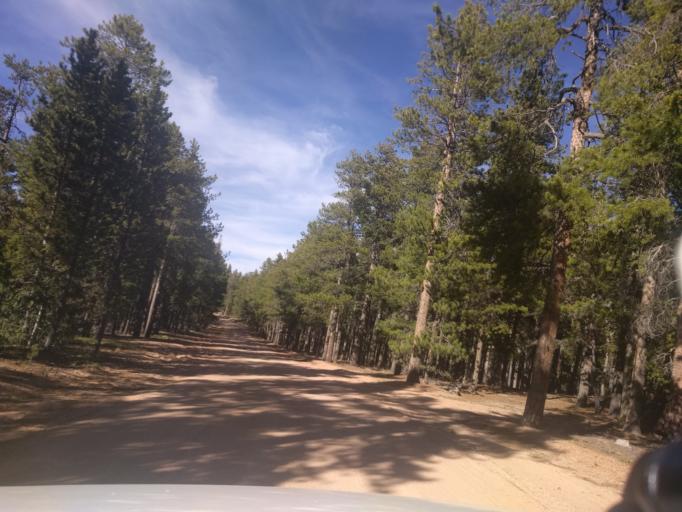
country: US
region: Colorado
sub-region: Douglas County
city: Perry Park
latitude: 39.2120
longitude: -105.0570
